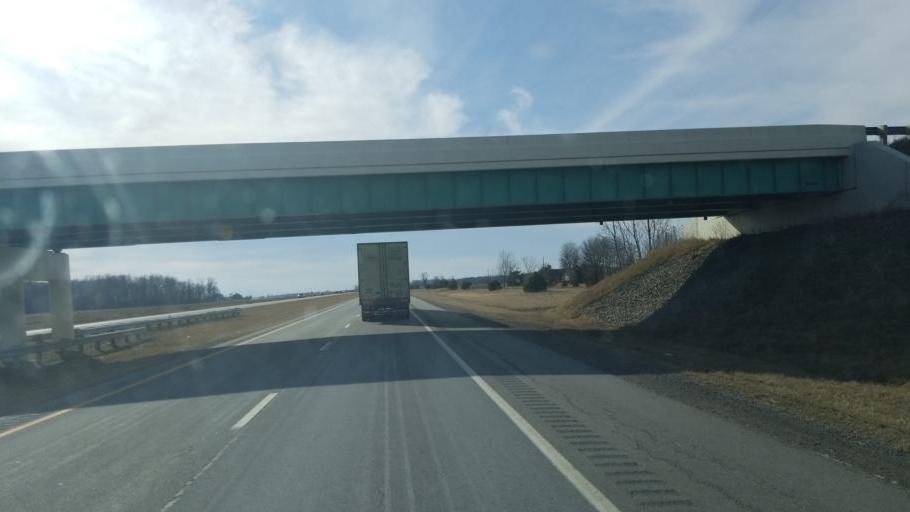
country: US
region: Ohio
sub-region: Allen County
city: Delphos
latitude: 40.8737
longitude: -84.3787
